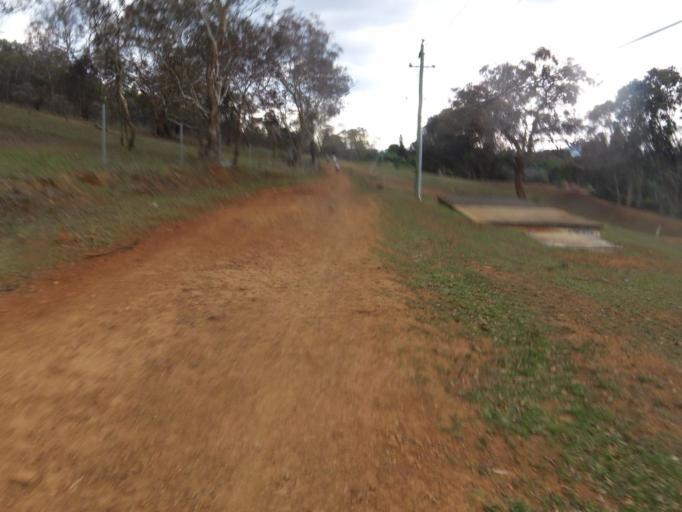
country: AU
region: Australian Capital Territory
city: Forrest
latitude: -35.3300
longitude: 149.1207
